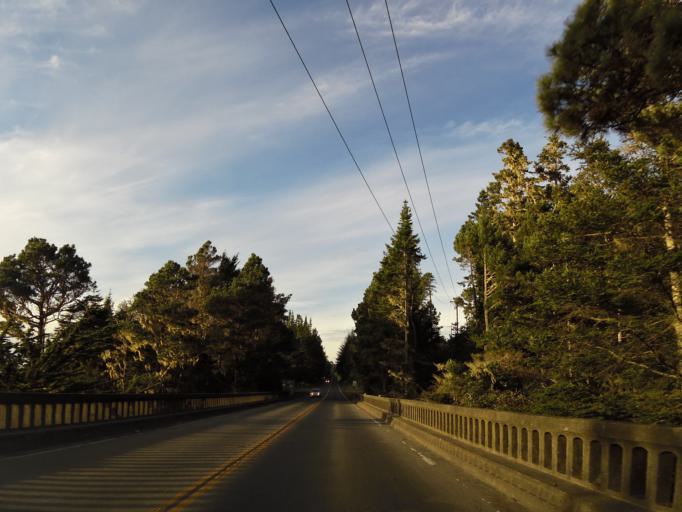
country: US
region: California
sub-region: Mendocino County
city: Fort Bragg
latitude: 39.3194
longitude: -123.8000
